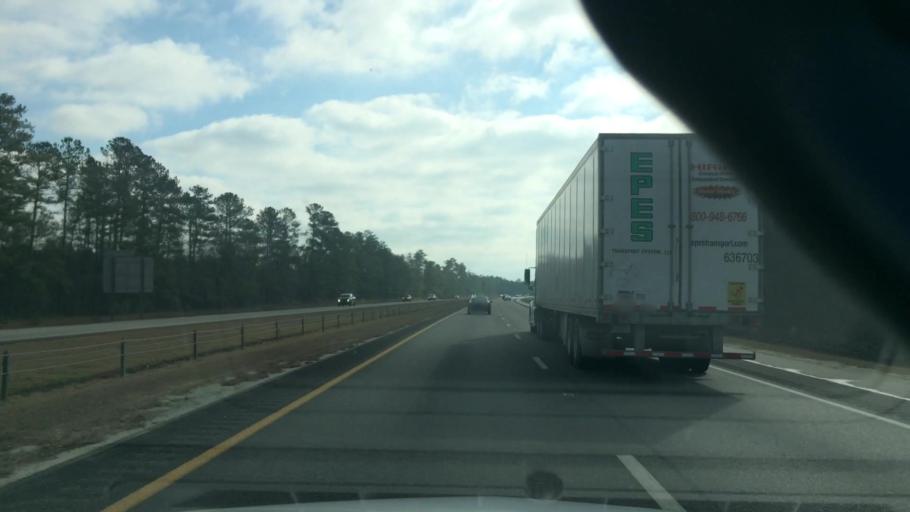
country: US
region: North Carolina
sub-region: Pender County
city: Burgaw
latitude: 34.5577
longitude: -77.8950
